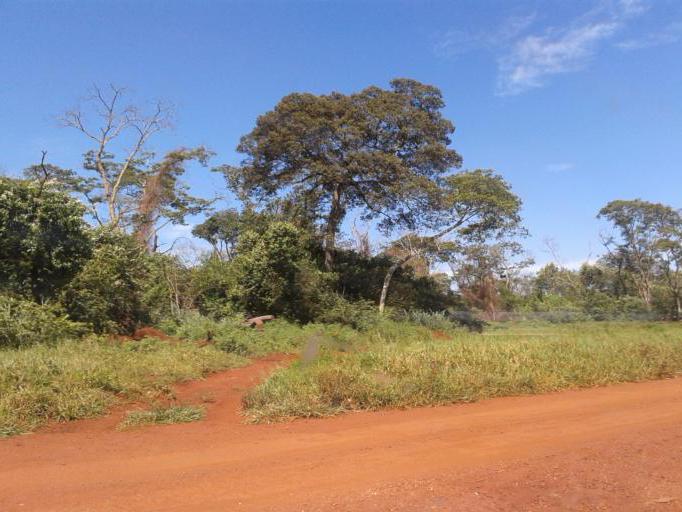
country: BR
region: Minas Gerais
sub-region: Capinopolis
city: Capinopolis
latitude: -18.6403
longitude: -49.6087
